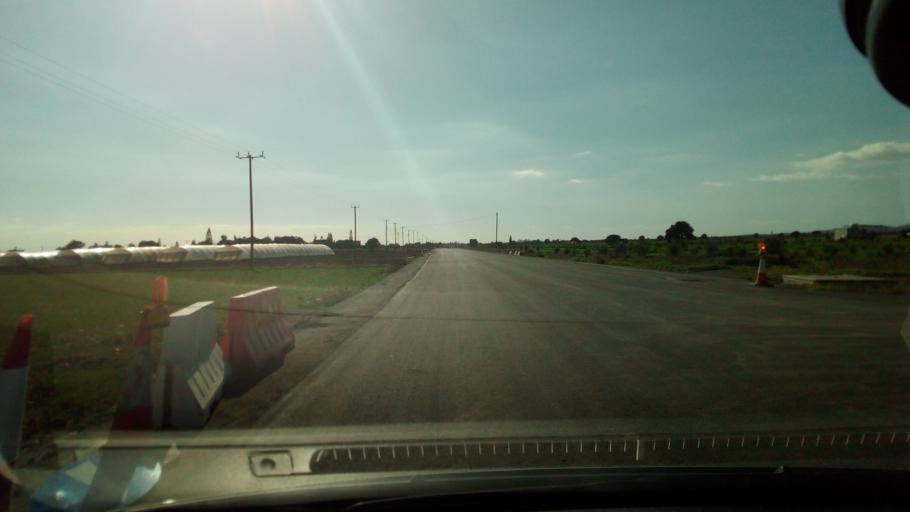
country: CY
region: Larnaka
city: Tersefanou
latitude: 34.8178
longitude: 33.5274
